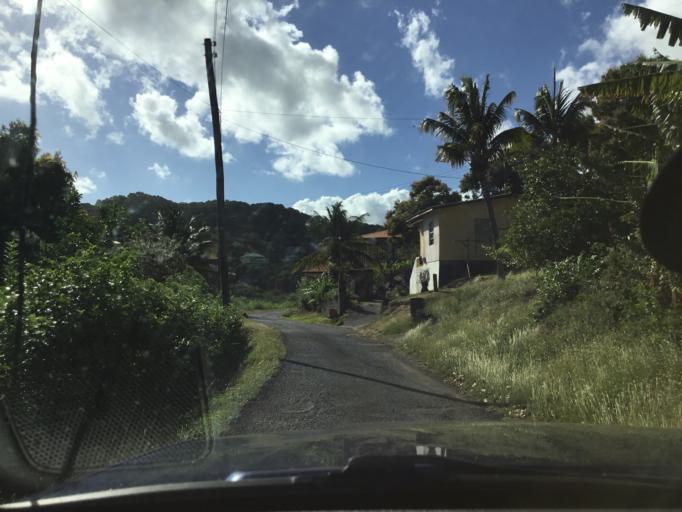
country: VC
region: Saint George
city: Kingstown
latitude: 13.1458
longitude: -61.1763
